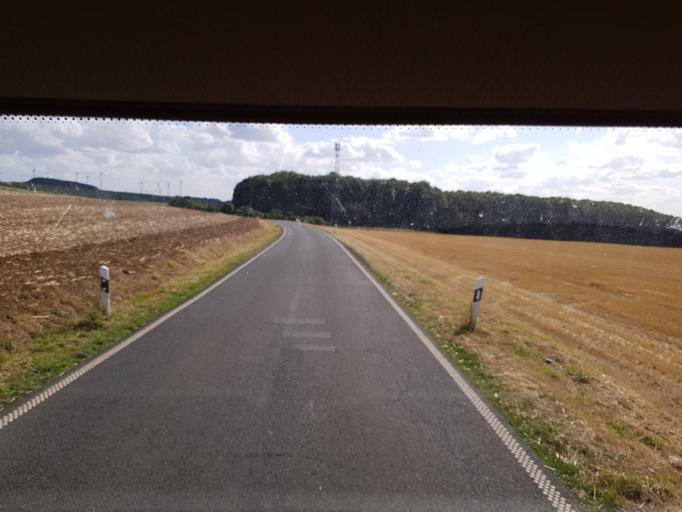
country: DE
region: Rheinland-Pfalz
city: Kirf
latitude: 49.5535
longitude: 6.4597
